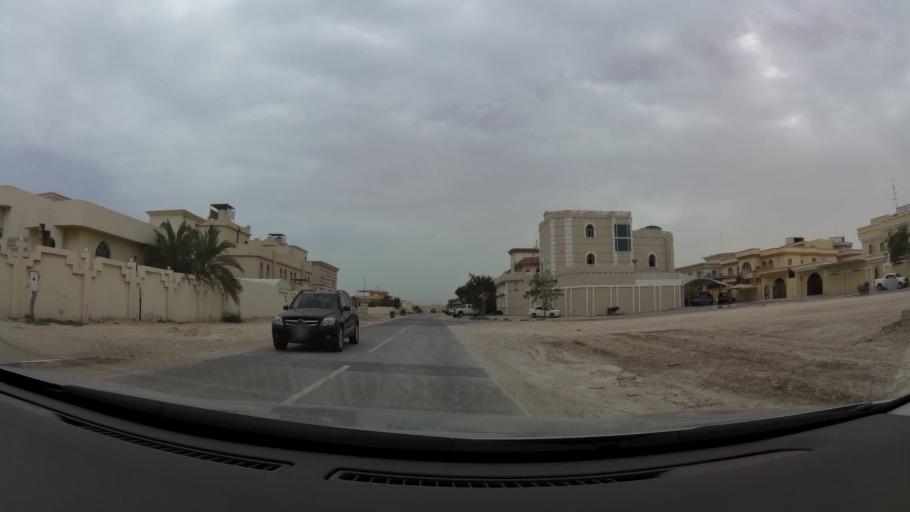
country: QA
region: Baladiyat ar Rayyan
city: Ar Rayyan
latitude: 25.3438
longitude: 51.4633
